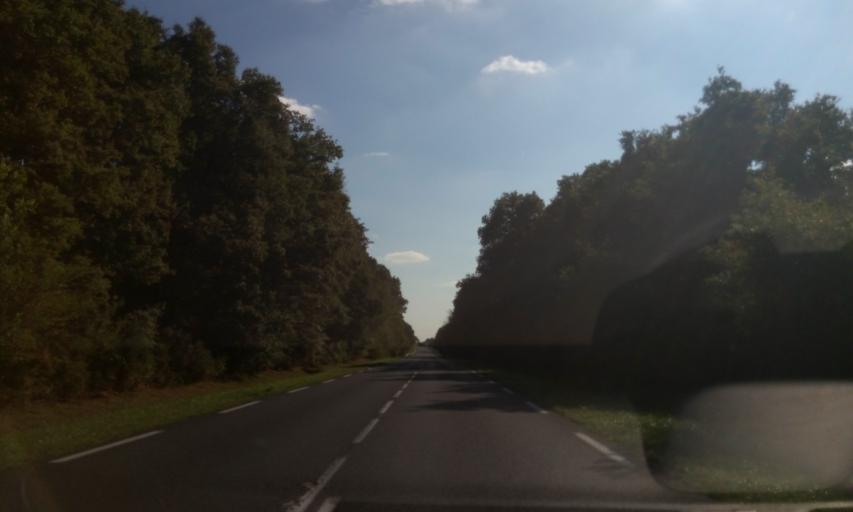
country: FR
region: Centre
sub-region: Departement d'Indre-et-Loire
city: Poce-sur-Cisse
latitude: 47.4705
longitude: 1.0076
